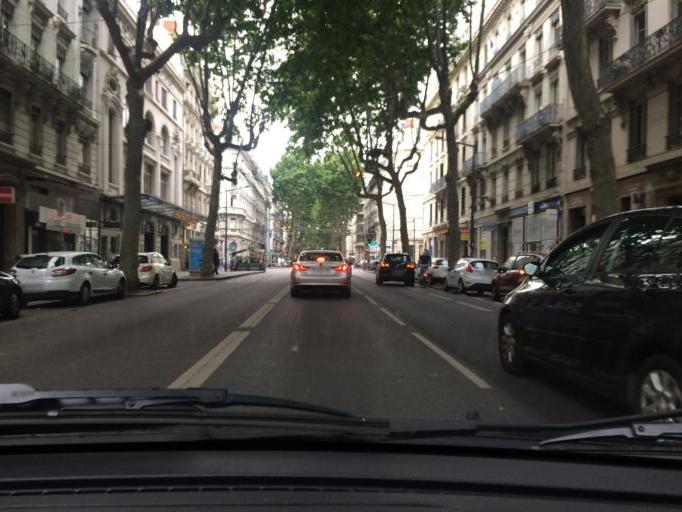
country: FR
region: Rhone-Alpes
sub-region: Departement du Rhone
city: Lyon
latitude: 45.7627
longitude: 4.8452
